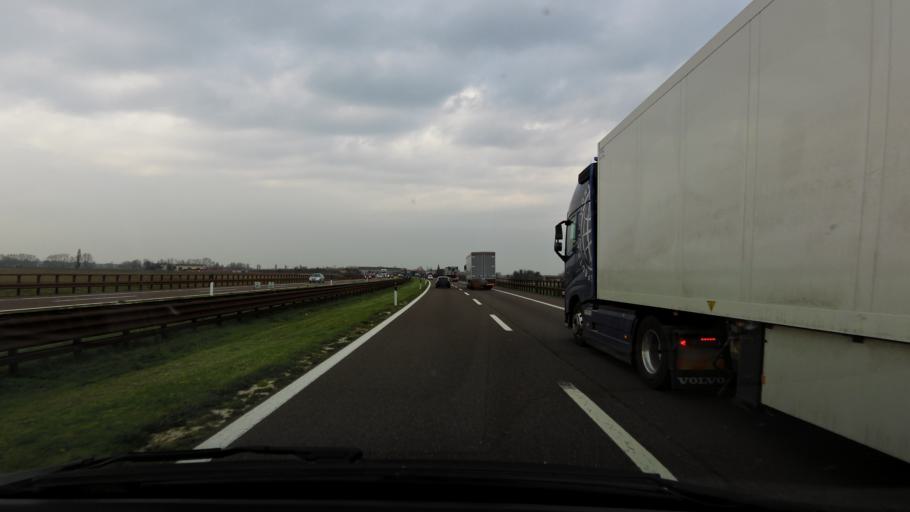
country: IT
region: Veneto
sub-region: Provincia di Verona
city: Vigasio
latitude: 45.3259
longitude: 10.9164
